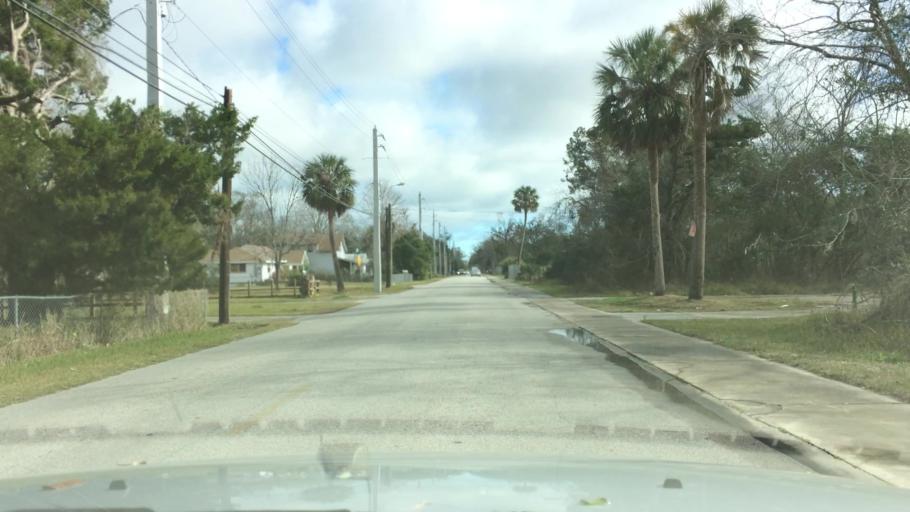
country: US
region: Florida
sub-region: Volusia County
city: Holly Hill
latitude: 29.2309
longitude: -81.0484
